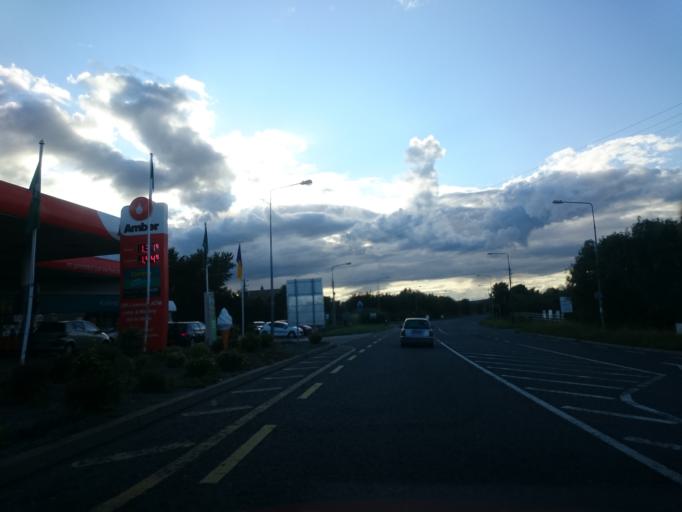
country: IE
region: Leinster
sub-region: Loch Garman
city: Rosslare
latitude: 52.2576
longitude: -6.4553
